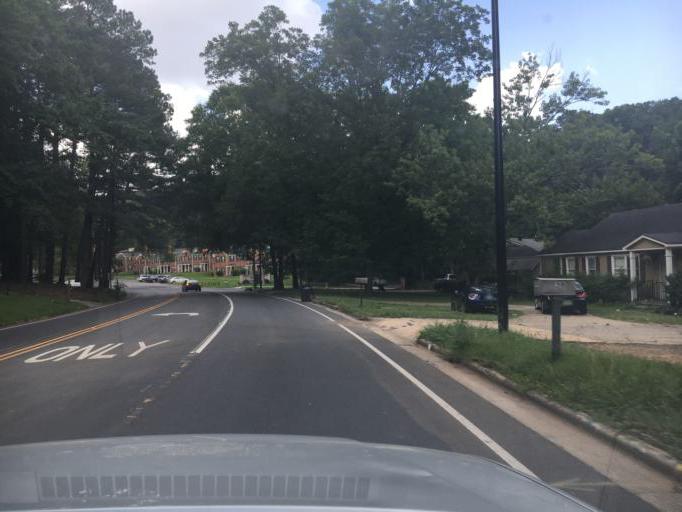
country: US
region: Alabama
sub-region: Jefferson County
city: Homewood
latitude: 33.4826
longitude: -86.8024
